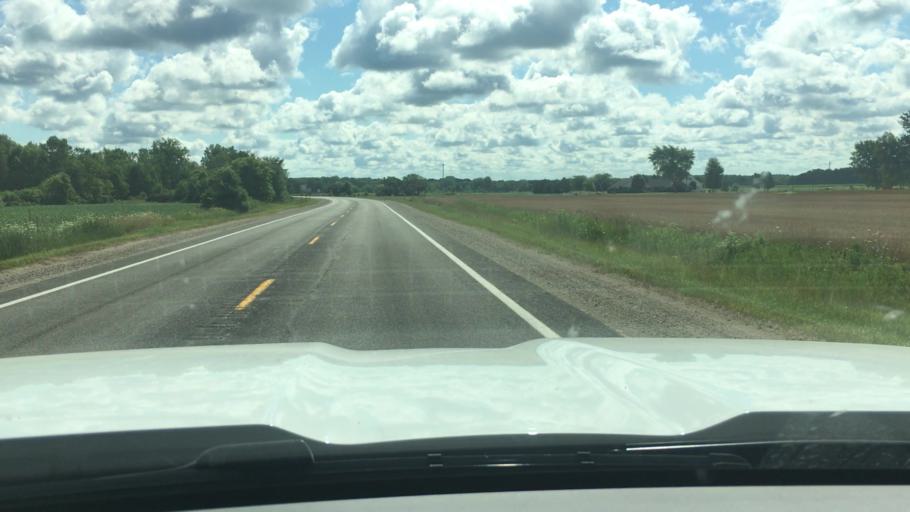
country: US
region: Michigan
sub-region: Clinton County
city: Ovid
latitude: 43.1759
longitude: -84.3723
